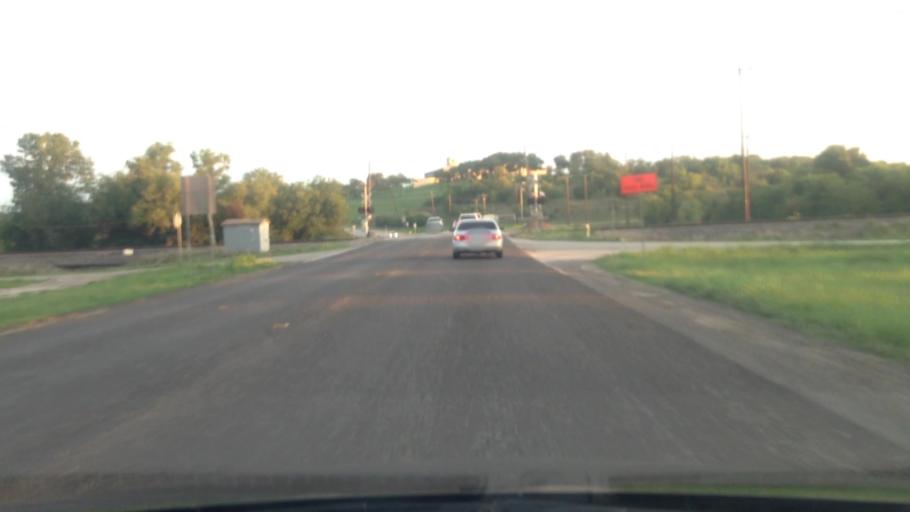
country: US
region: Texas
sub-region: Tarrant County
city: Benbrook
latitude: 32.6791
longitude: -97.4988
